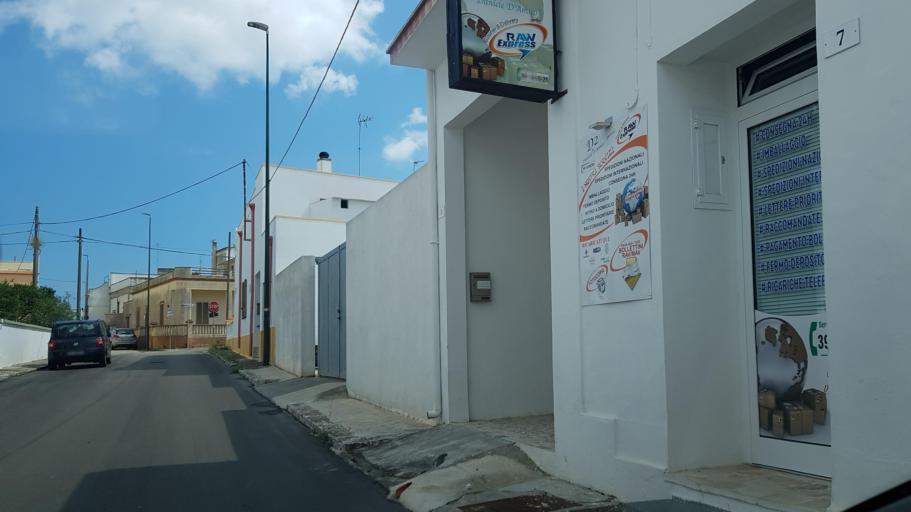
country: IT
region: Apulia
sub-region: Provincia di Lecce
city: Castrignano del Capo
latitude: 39.8329
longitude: 18.3529
